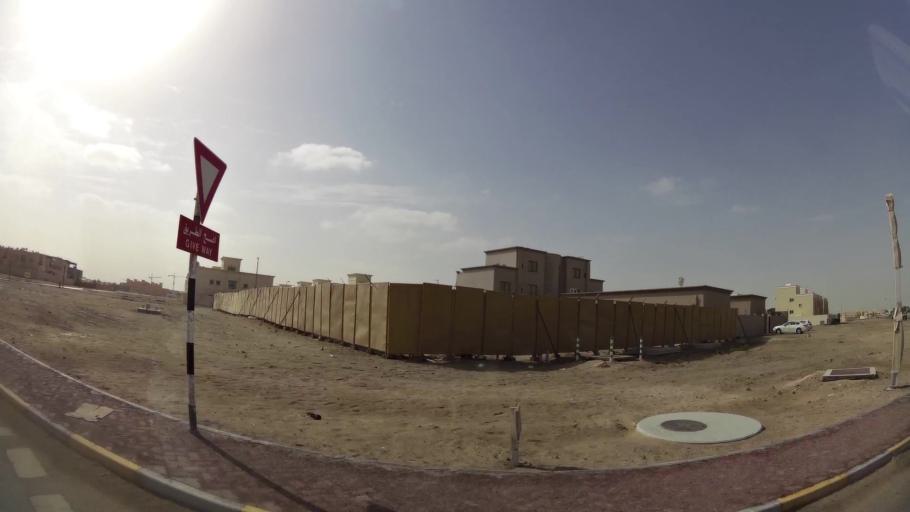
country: AE
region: Abu Dhabi
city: Abu Dhabi
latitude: 24.4332
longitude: 54.5919
